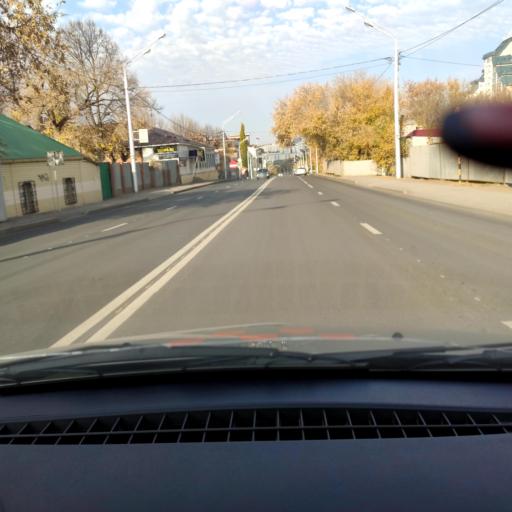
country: RU
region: Bashkortostan
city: Ufa
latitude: 54.7059
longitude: 55.9778
